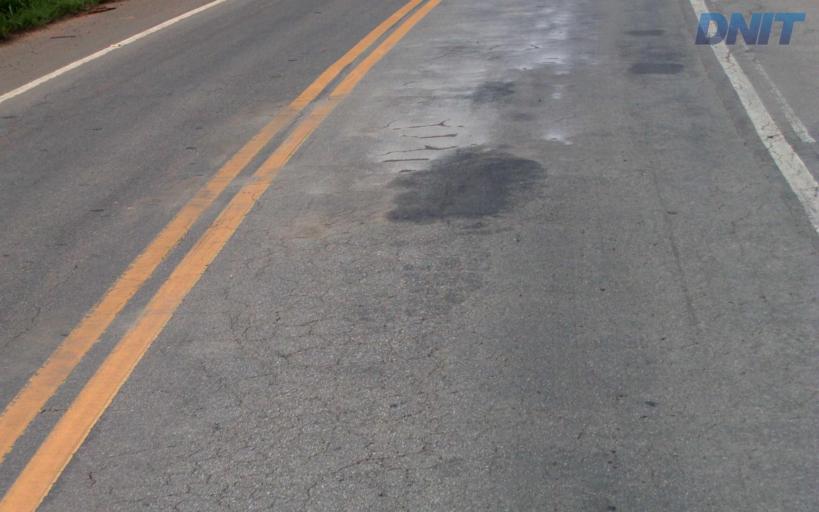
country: BR
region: Minas Gerais
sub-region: Ipaba
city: Ipaba
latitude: -19.3248
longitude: -42.4184
